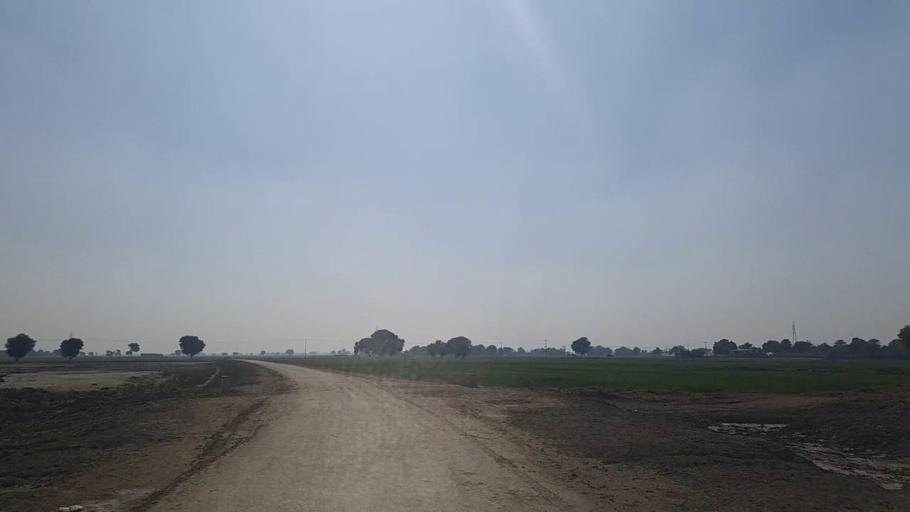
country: PK
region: Sindh
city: Shahpur Chakar
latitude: 26.1934
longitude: 68.5440
